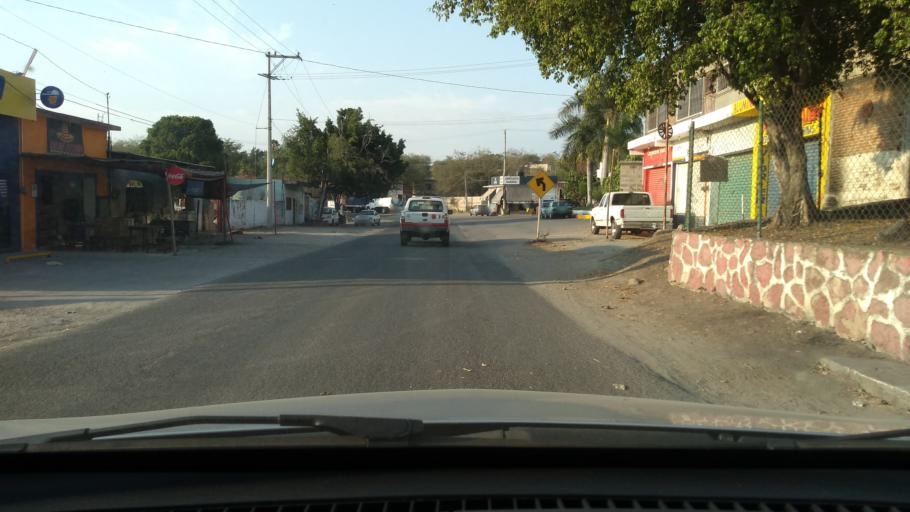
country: MX
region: Morelos
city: Puente de Ixtla
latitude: 18.6130
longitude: -99.3121
